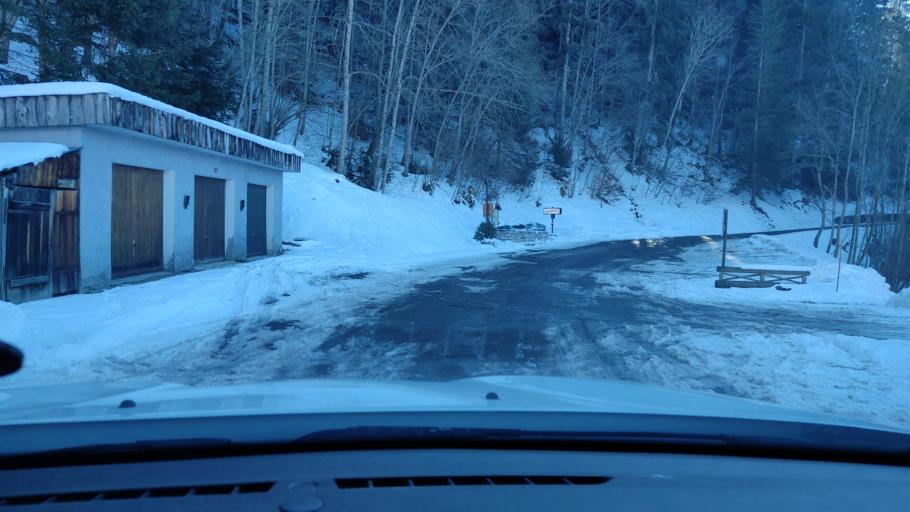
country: FR
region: Rhone-Alpes
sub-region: Departement de la Savoie
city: Les Allues
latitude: 45.4319
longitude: 6.5694
